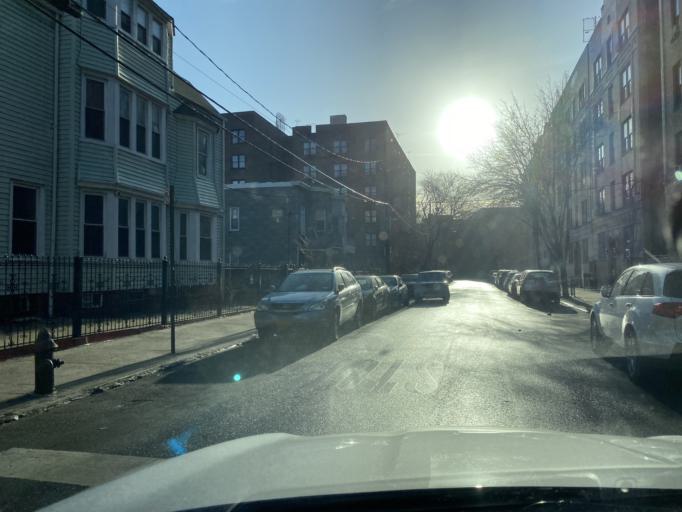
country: US
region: New York
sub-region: Bronx
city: The Bronx
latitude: 40.8702
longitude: -73.8872
